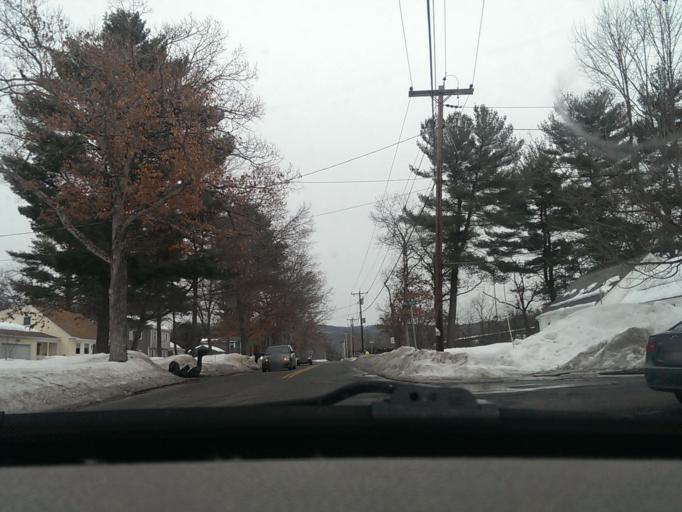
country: US
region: Massachusetts
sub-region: Hampden County
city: Wilbraham
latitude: 42.0940
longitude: -72.4572
